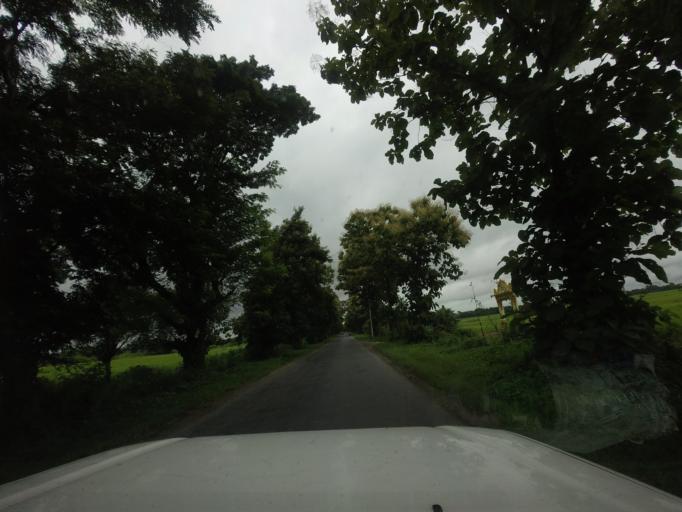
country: MM
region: Ayeyarwady
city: Hinthada
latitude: 17.6145
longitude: 95.4803
